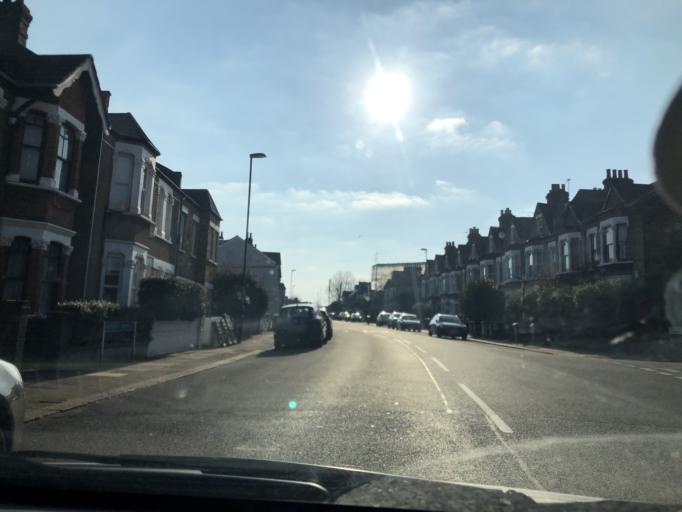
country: GB
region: England
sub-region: Greater London
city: Catford
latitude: 51.4552
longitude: -0.0318
